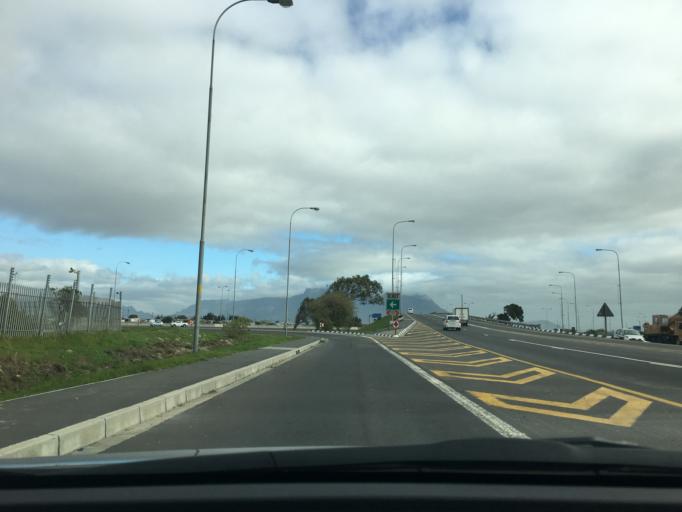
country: ZA
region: Western Cape
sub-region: City of Cape Town
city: Lansdowne
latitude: -33.9680
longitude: 18.5766
